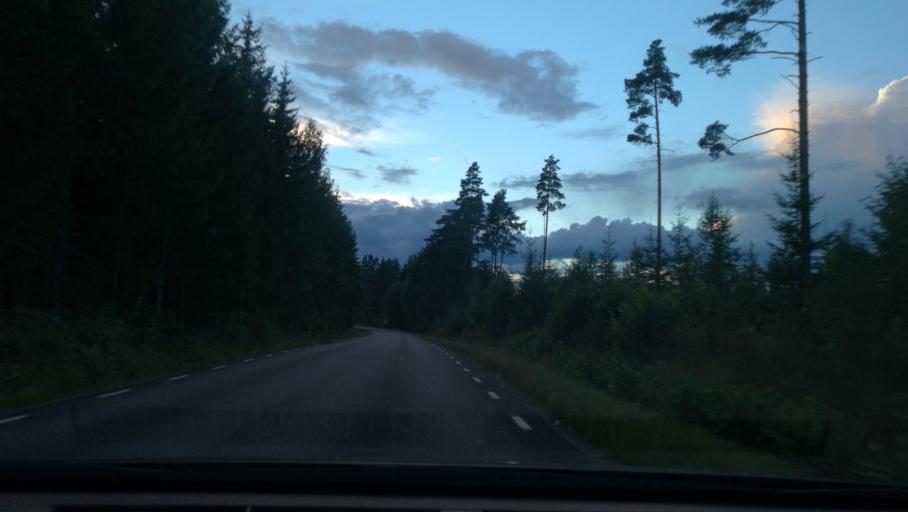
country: SE
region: OEstergoetland
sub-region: Norrkopings Kommun
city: Svartinge
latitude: 58.8209
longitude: 15.9998
